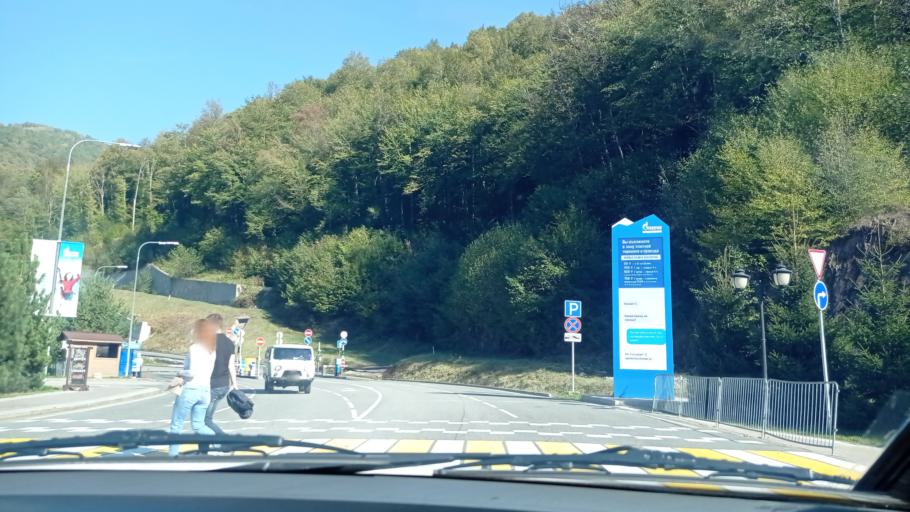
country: RU
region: Krasnodarskiy
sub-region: Sochi City
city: Krasnaya Polyana
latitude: 43.6823
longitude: 40.2794
